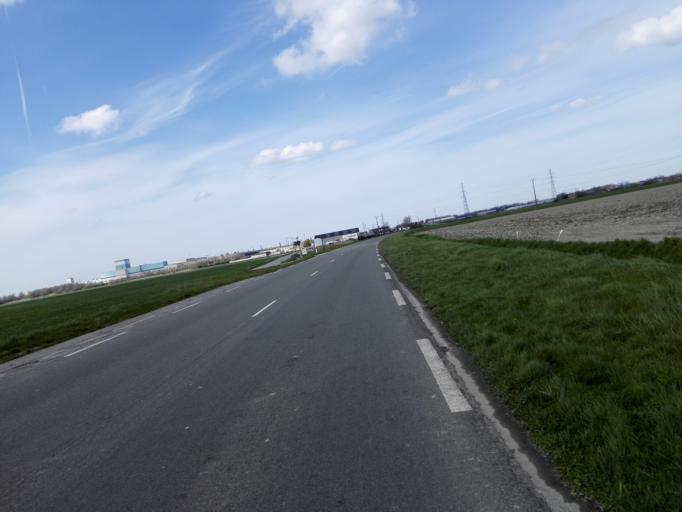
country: FR
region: Nord-Pas-de-Calais
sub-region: Departement du Nord
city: Spycker
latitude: 50.9775
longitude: 2.3086
